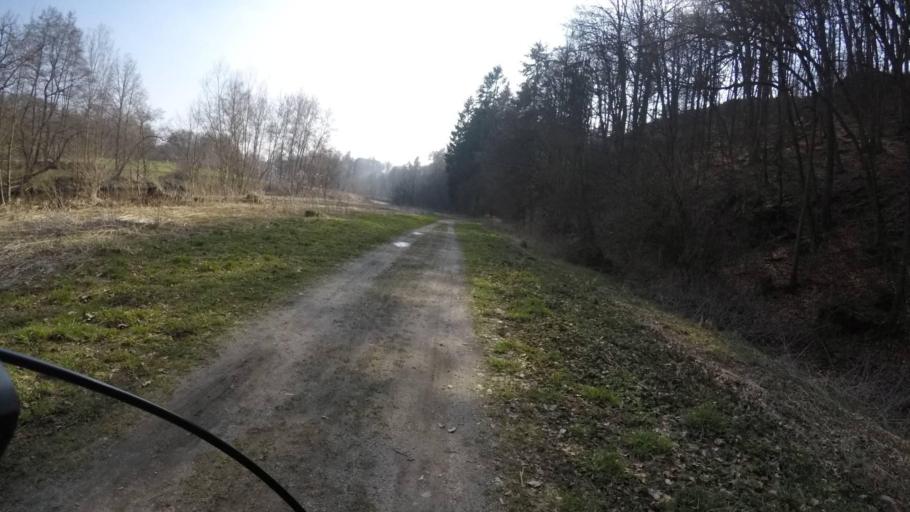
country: DE
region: Saxony
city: Penig
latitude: 50.9099
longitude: 12.6728
